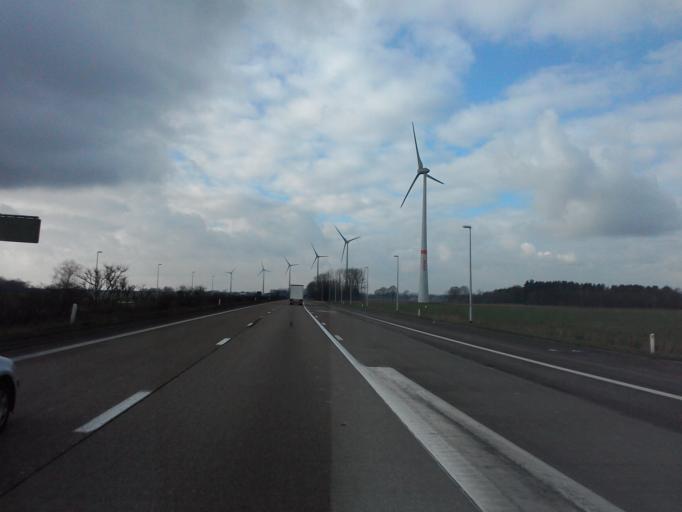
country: BE
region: Flanders
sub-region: Provincie Antwerpen
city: Arendonk
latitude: 51.2956
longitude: 5.0875
